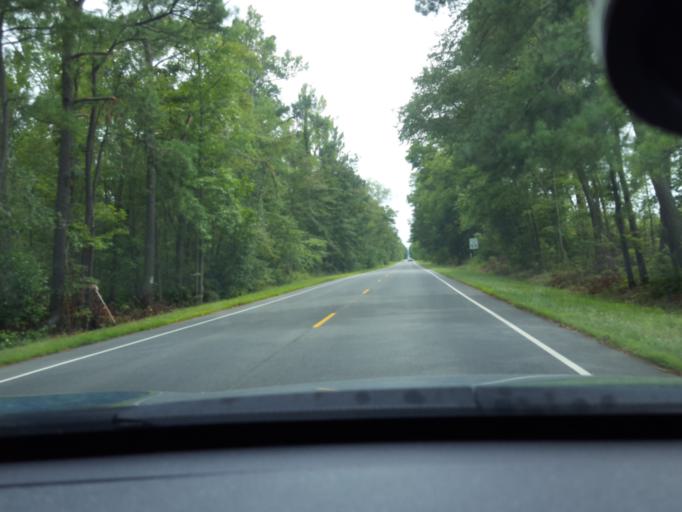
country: US
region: Virginia
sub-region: Caroline County
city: Bowling Green
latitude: 37.9716
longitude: -77.3413
